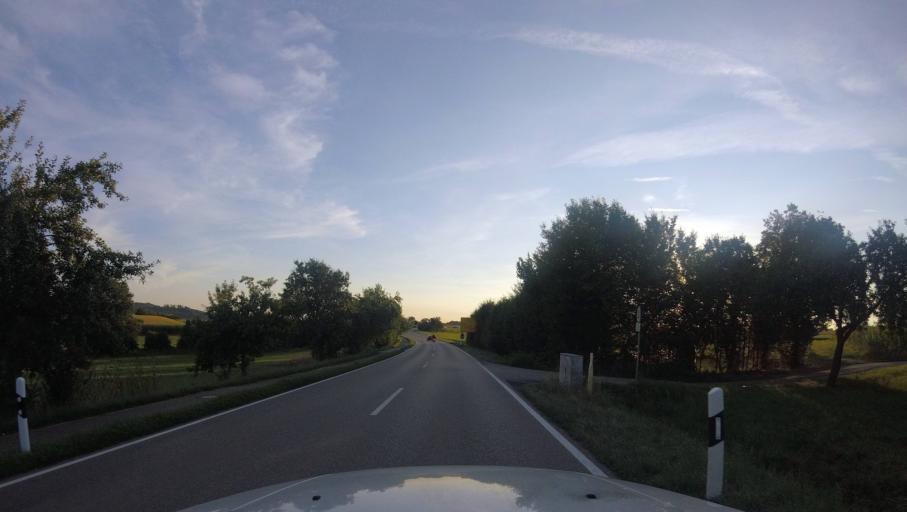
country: DE
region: Baden-Wuerttemberg
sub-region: Regierungsbezirk Stuttgart
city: Allmersbach im Tal
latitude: 48.9259
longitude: 9.4585
